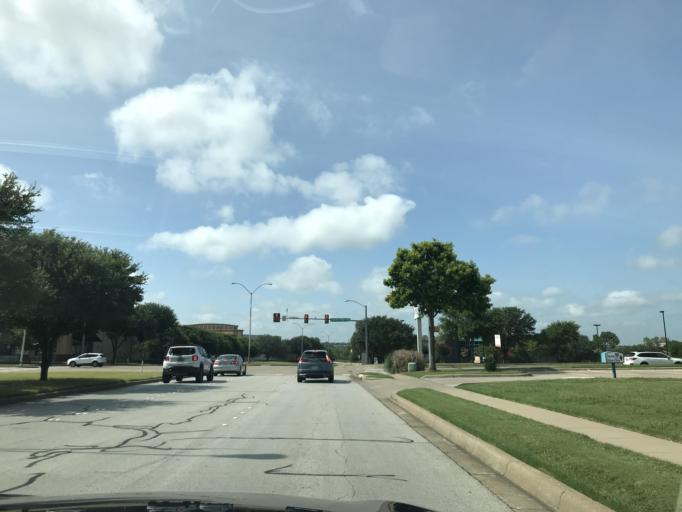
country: US
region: Texas
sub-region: Tarrant County
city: Benbrook
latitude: 32.6773
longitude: -97.4034
